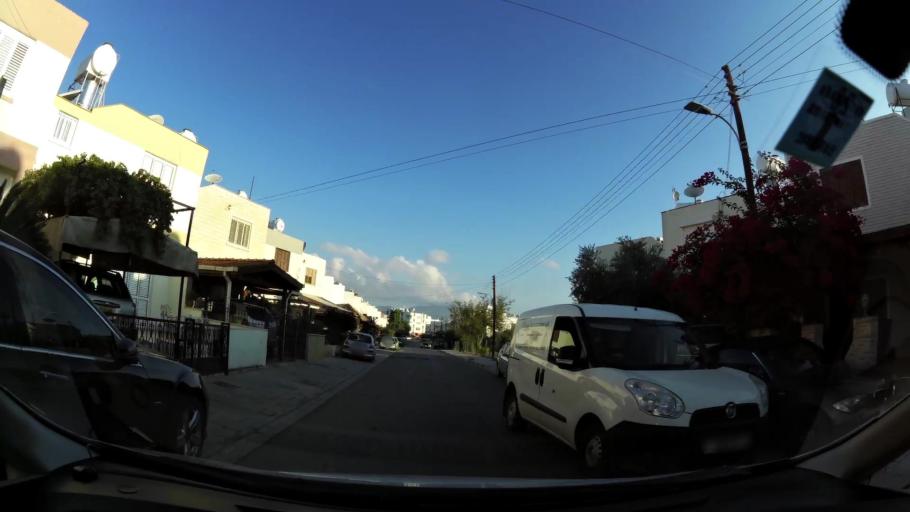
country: CY
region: Lefkosia
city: Nicosia
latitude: 35.1974
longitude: 33.3264
